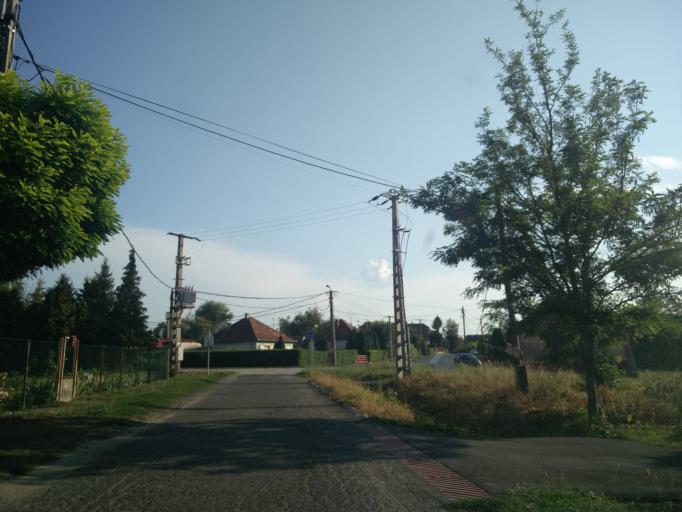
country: HU
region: Zala
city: Zalaegerszeg
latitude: 46.8475
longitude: 16.8757
